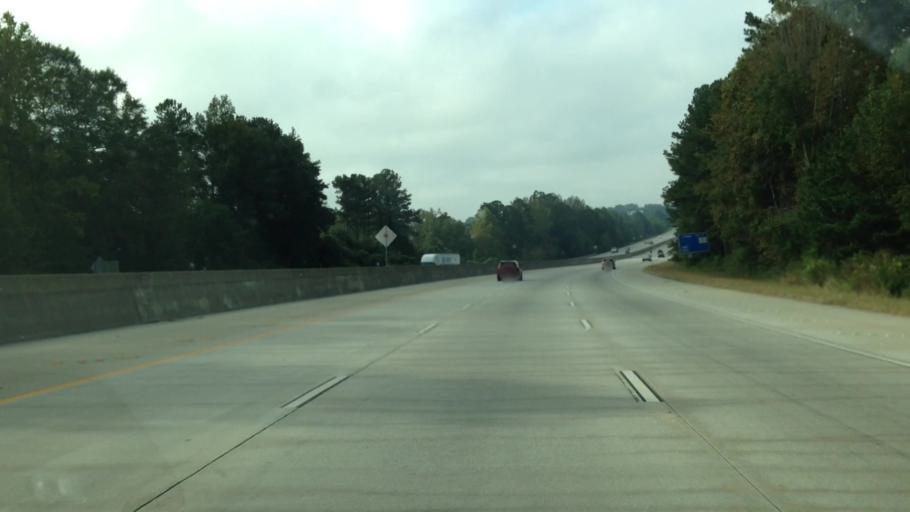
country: US
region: Georgia
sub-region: Coweta County
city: East Newnan
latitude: 33.3471
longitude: -84.7613
